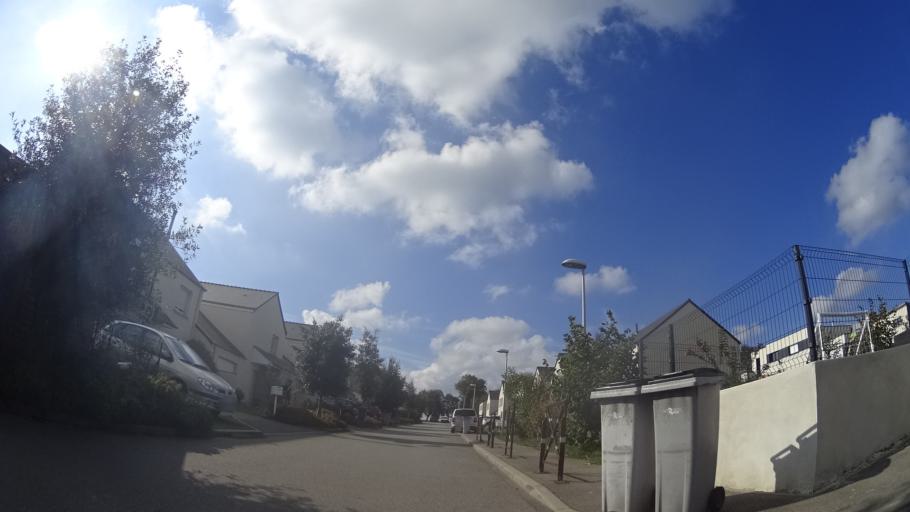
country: FR
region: Brittany
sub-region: Departement d'Ille-et-Vilaine
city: Geveze
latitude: 48.2238
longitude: -1.8026
